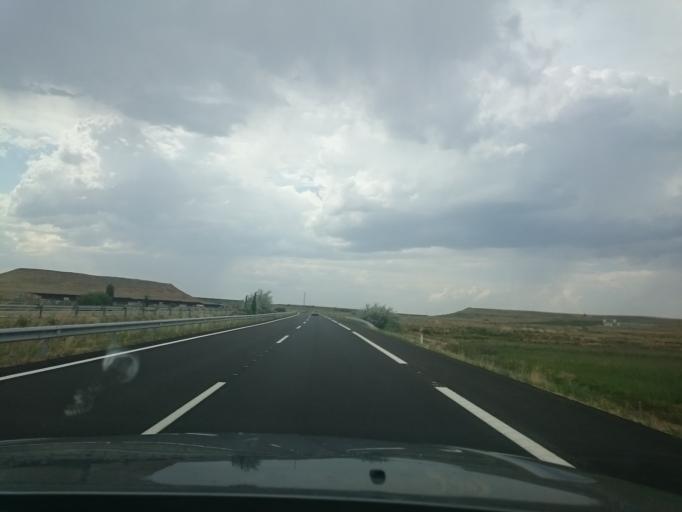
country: ES
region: La Rioja
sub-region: Provincia de La Rioja
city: Rincon de Soto
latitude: 42.1986
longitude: -1.8520
